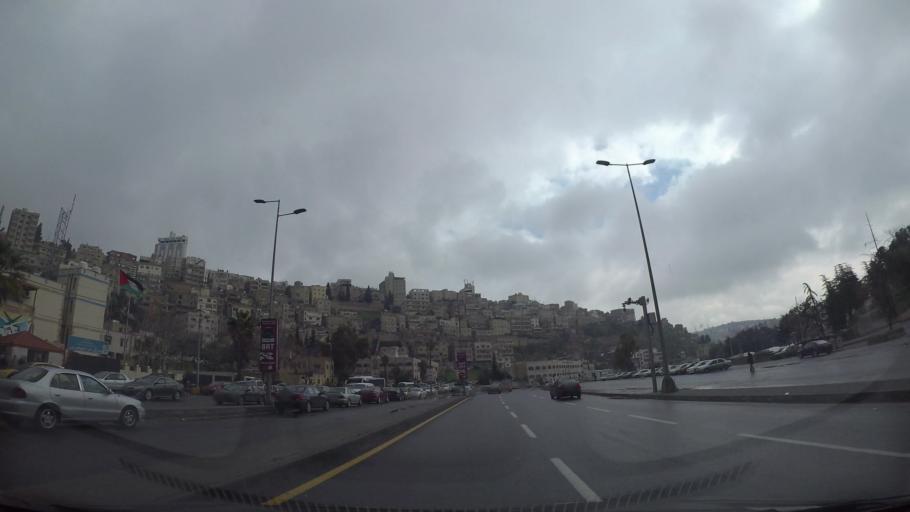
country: JO
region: Amman
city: Amman
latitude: 31.9481
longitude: 35.9136
